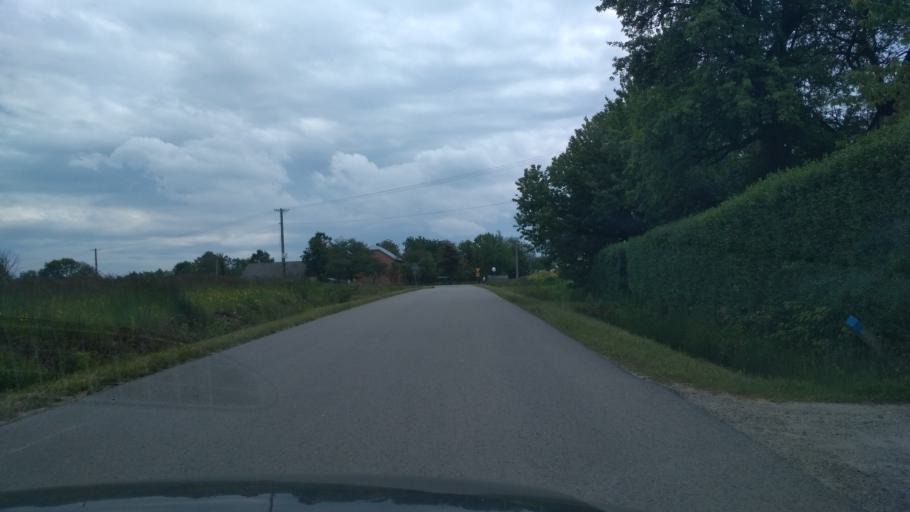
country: PL
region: Subcarpathian Voivodeship
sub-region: Powiat ropczycko-sedziszowski
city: Wielopole Skrzynskie
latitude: 49.9796
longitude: 21.6253
